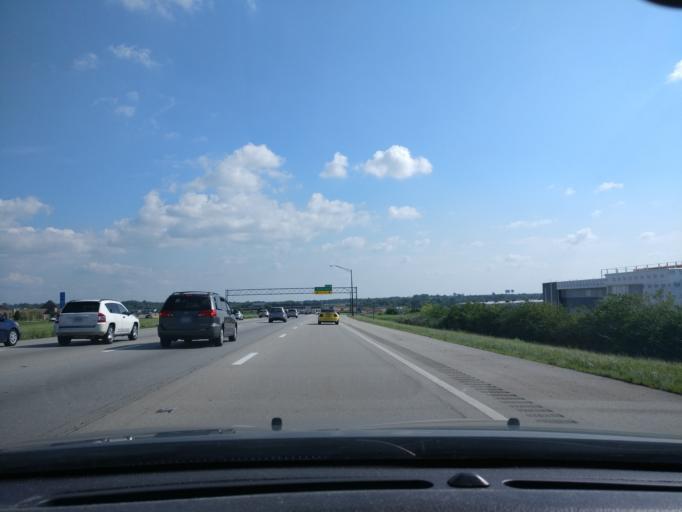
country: US
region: Ohio
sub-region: Warren County
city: Springboro
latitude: 39.6022
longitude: -84.2367
